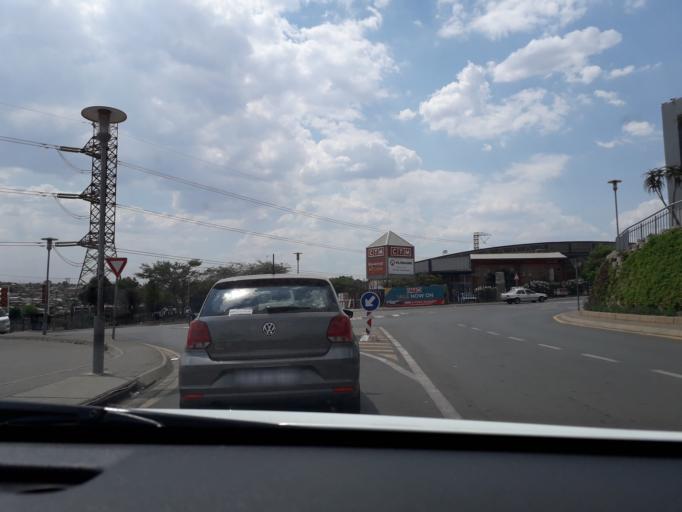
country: ZA
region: Gauteng
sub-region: Ekurhuleni Metropolitan Municipality
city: Tembisa
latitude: -26.0369
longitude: 28.1920
